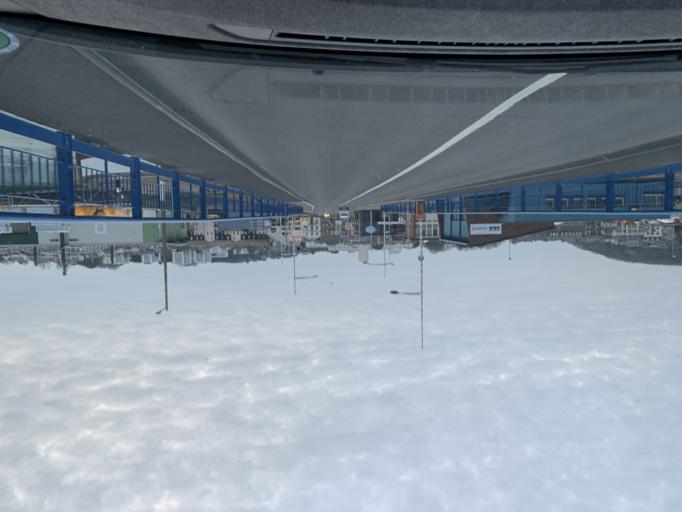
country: FR
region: Haute-Normandie
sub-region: Departement de la Seine-Maritime
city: Fecamp
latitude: 49.7618
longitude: 0.3743
